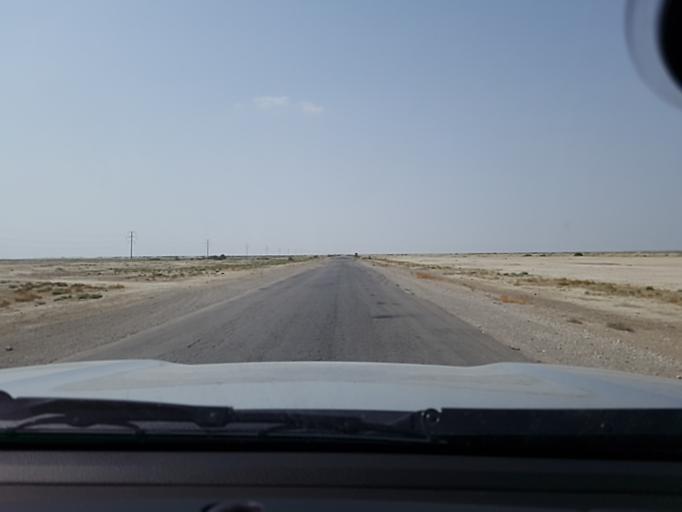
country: TM
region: Balkan
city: Gumdag
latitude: 38.9101
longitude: 54.5915
